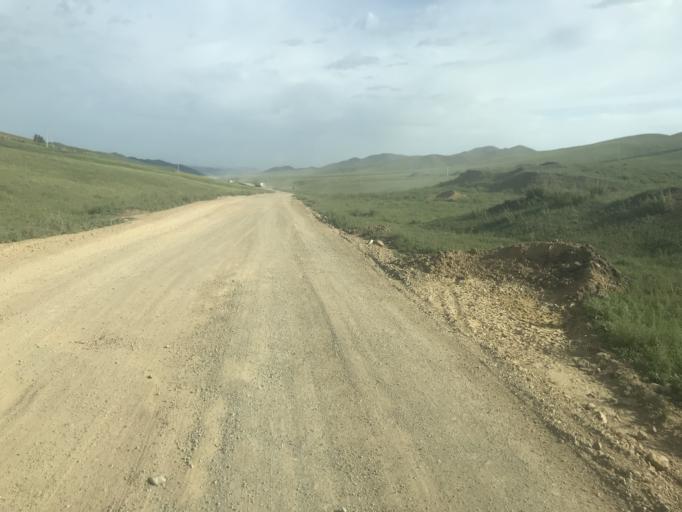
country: MN
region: Central Aimak
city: Javhlant
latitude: 48.7316
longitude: 106.1337
